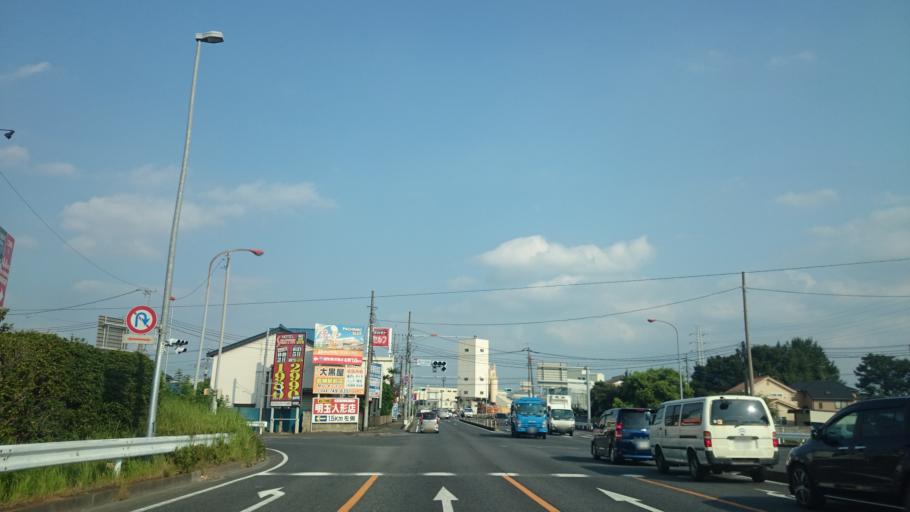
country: JP
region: Saitama
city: Iwatsuki
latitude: 35.9409
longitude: 139.6799
